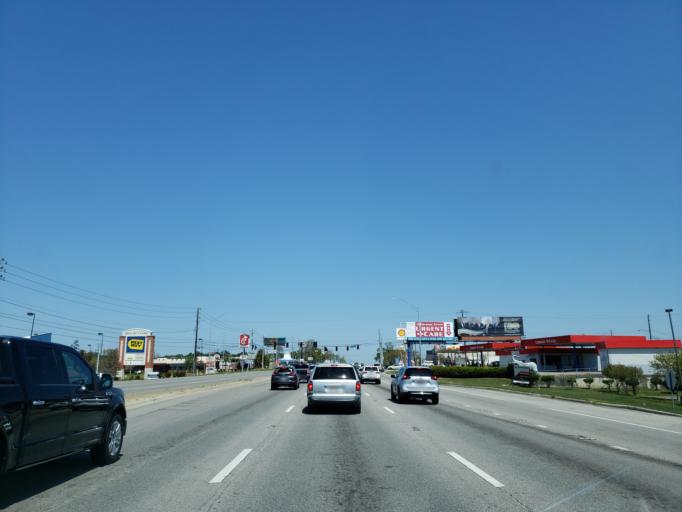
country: US
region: Mississippi
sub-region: Harrison County
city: West Gulfport
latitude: 30.4406
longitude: -89.0978
